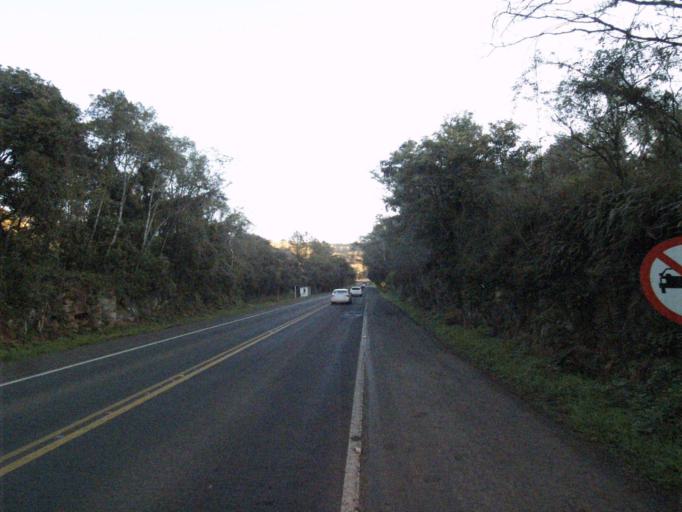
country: BR
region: Santa Catarina
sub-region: Sao Lourenco Do Oeste
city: Sao Lourenco dOeste
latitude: -26.8256
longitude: -53.1065
